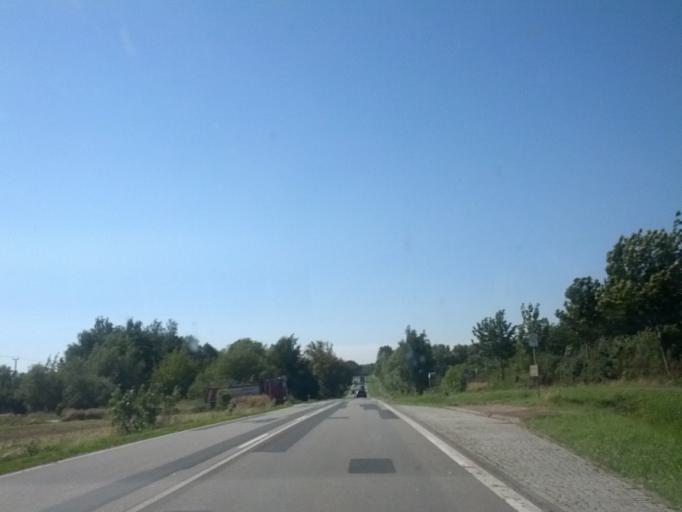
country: DE
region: Mecklenburg-Vorpommern
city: Sagard
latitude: 54.5044
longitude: 13.5303
